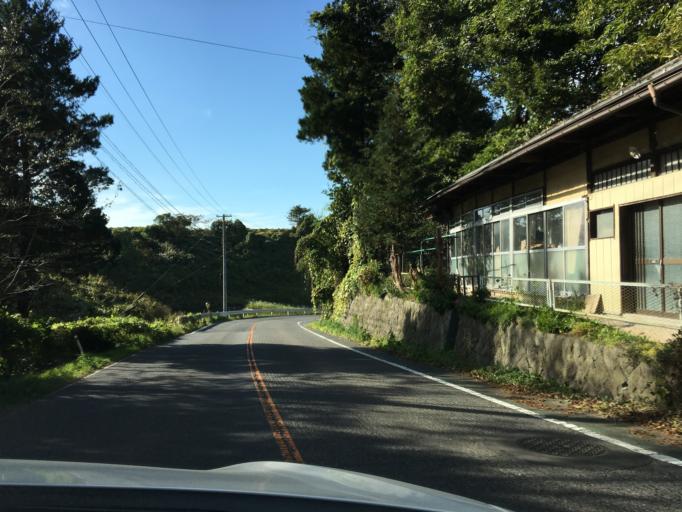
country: JP
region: Fukushima
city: Miharu
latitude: 37.3599
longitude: 140.5061
